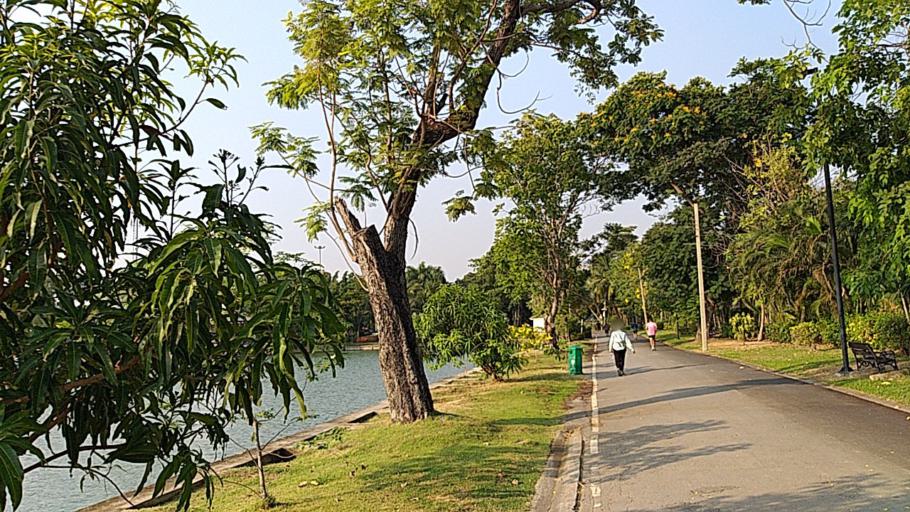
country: TH
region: Bangkok
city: Don Mueang
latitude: 13.9310
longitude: 100.5544
